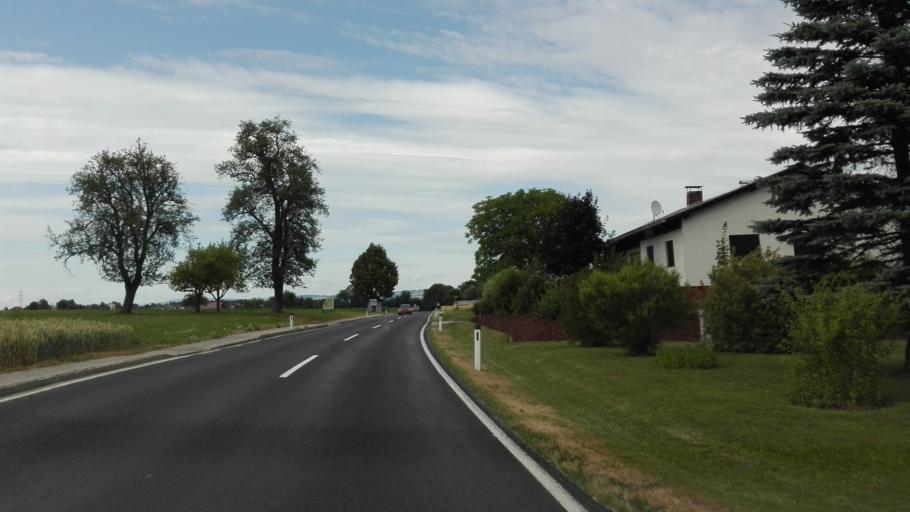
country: AT
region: Upper Austria
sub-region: Politischer Bezirk Grieskirchen
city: Grieskirchen
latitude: 48.2633
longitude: 13.8135
